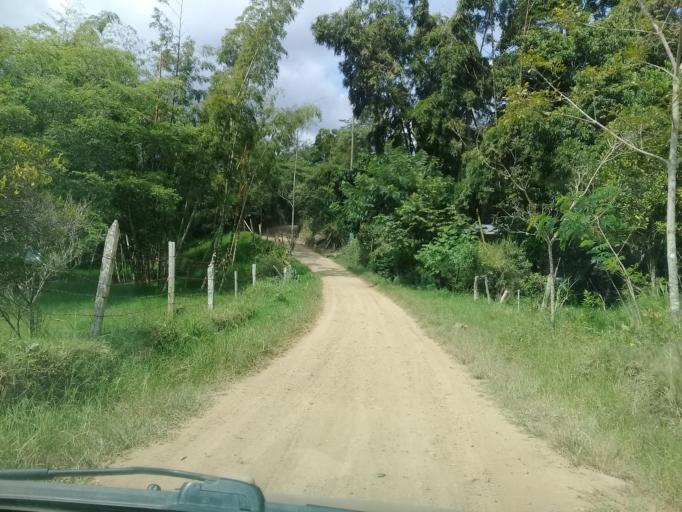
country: CO
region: Cundinamarca
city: Guaduas
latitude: 5.0413
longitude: -74.6088
